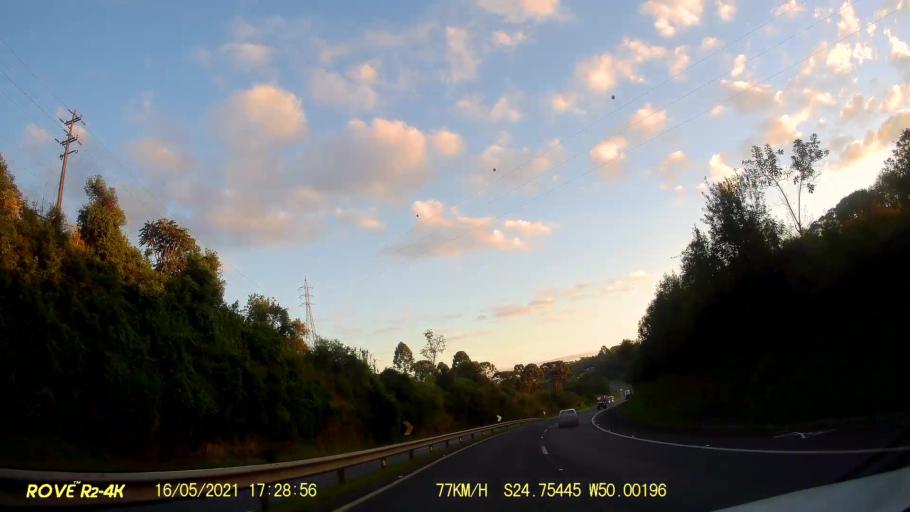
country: BR
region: Parana
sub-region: Castro
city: Castro
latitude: -24.7548
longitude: -50.0021
